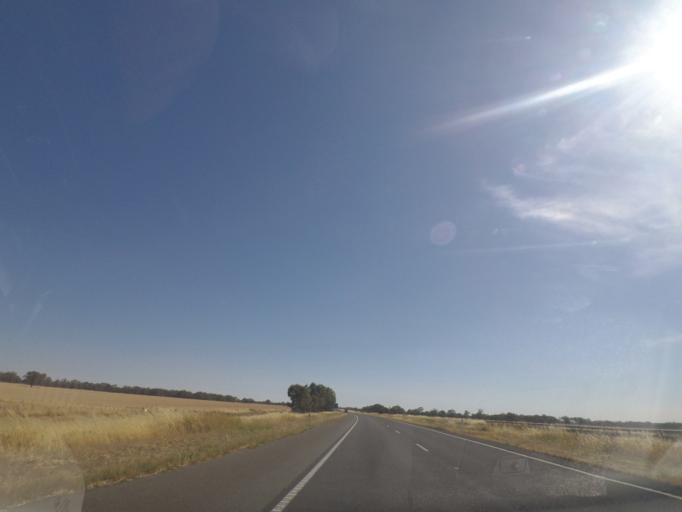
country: AU
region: Victoria
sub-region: Greater Shepparton
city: Shepparton
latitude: -36.6219
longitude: 145.3033
